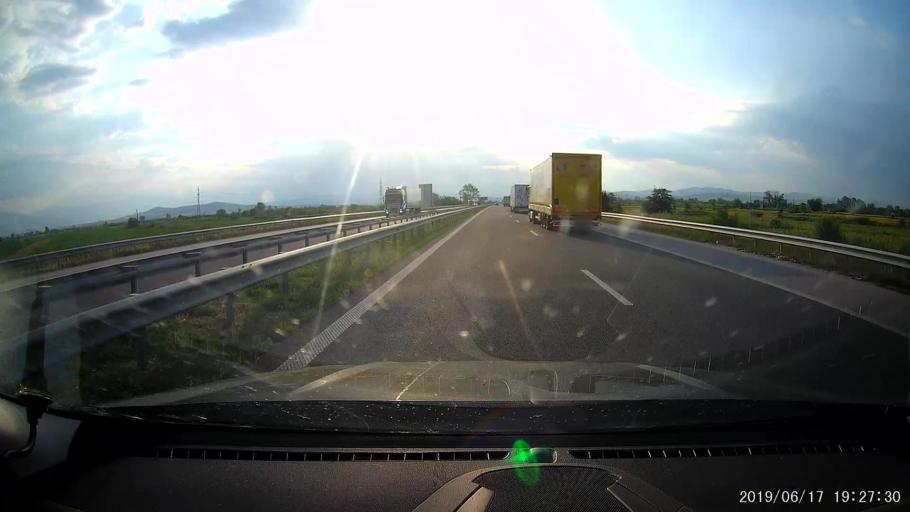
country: BG
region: Pazardzhik
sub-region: Obshtina Pazardzhik
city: Pazardzhik
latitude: 42.2667
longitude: 24.3034
